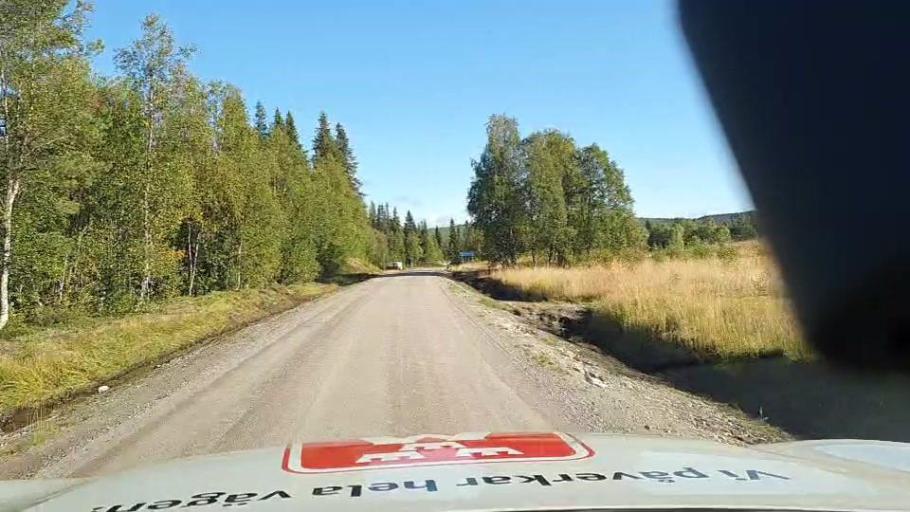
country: SE
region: Jaemtland
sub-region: Stroemsunds Kommun
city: Stroemsund
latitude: 64.5080
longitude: 15.1462
